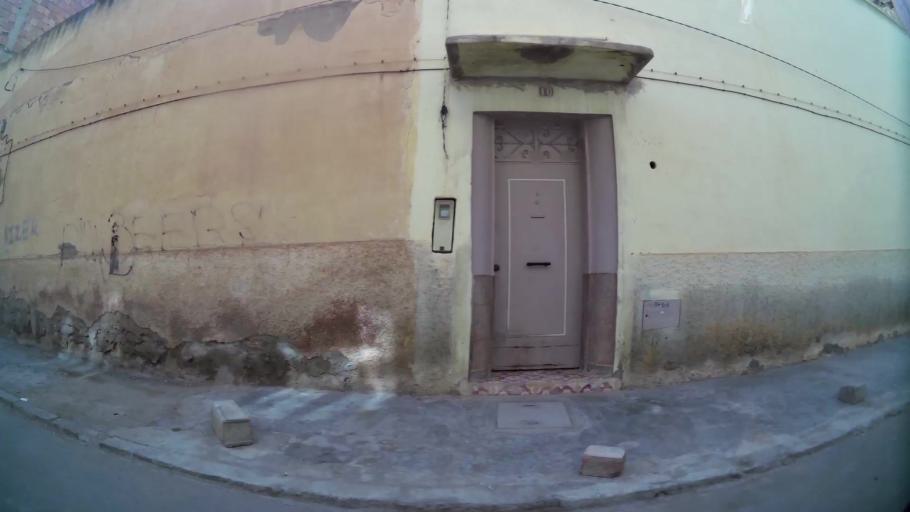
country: MA
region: Oriental
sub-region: Oujda-Angad
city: Oujda
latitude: 34.6876
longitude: -1.9087
